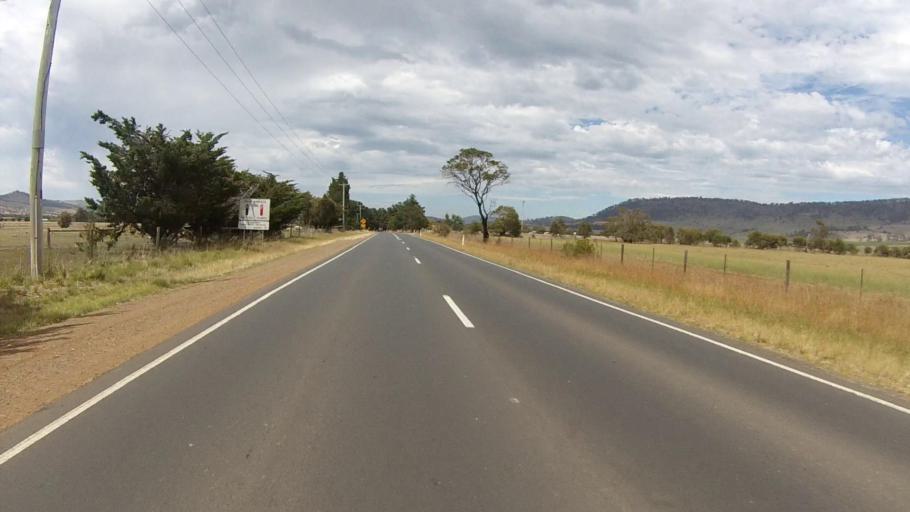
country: AU
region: Tasmania
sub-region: Clarence
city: Cambridge
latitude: -42.6843
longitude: 147.4301
